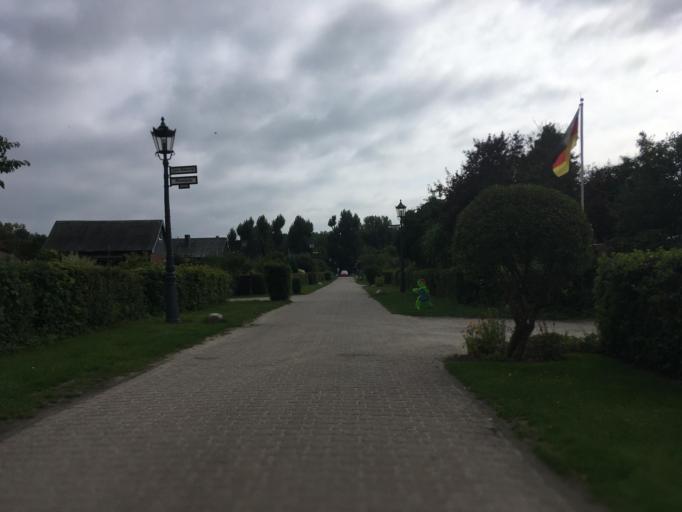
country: DE
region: Berlin
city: Konradshohe
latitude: 52.6034
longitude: 13.2212
